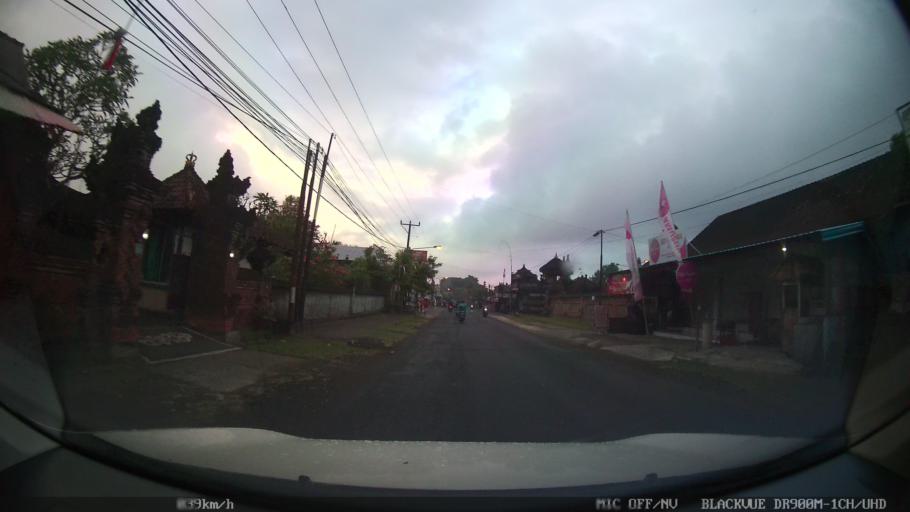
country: ID
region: Bali
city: Banjar Parekan
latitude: -8.5734
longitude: 115.2186
